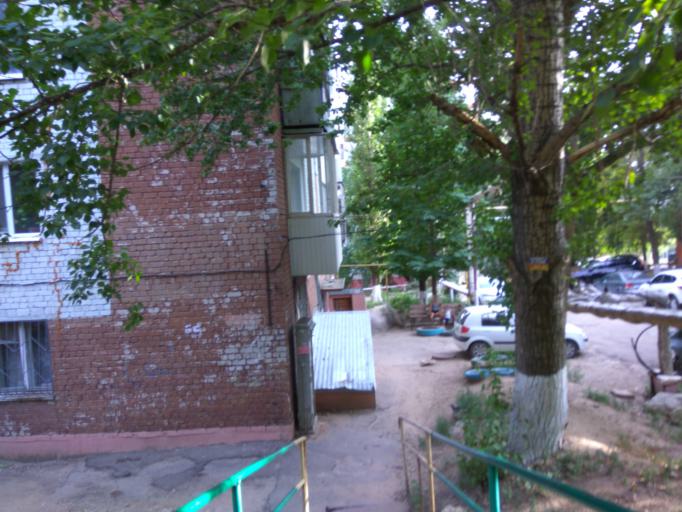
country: RU
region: Saratov
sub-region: Saratovskiy Rayon
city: Saratov
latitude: 51.5512
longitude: 46.0534
